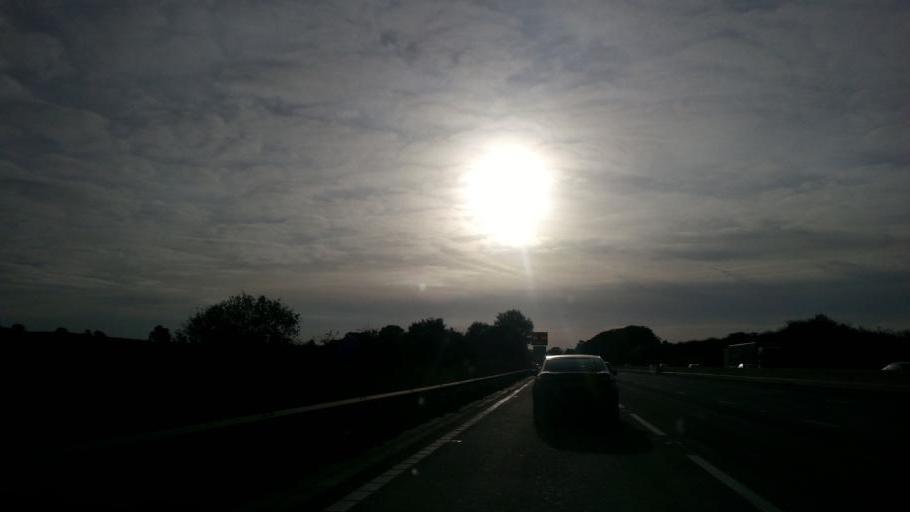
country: GB
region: England
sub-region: Northamptonshire
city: Bugbrooke
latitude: 52.2369
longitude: -1.0395
